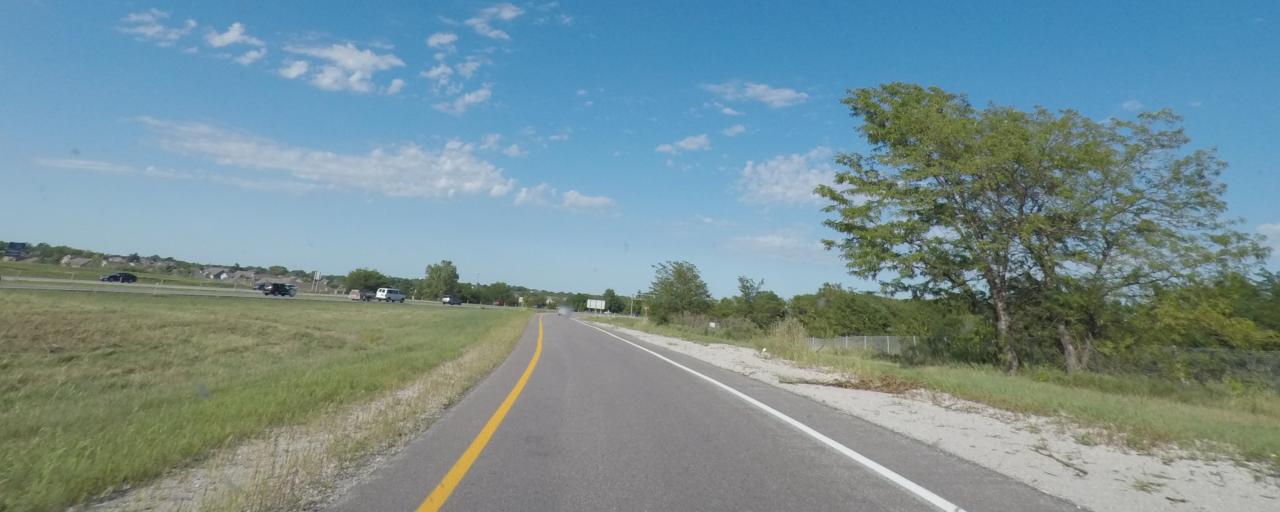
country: US
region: Missouri
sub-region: Clay County
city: Gladstone
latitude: 39.2566
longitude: -94.5984
